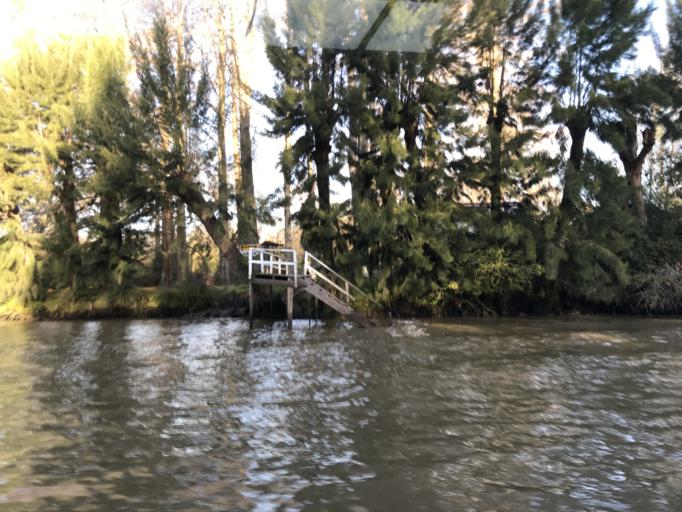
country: AR
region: Buenos Aires
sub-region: Partido de Tigre
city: Tigre
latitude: -34.3735
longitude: -58.5856
